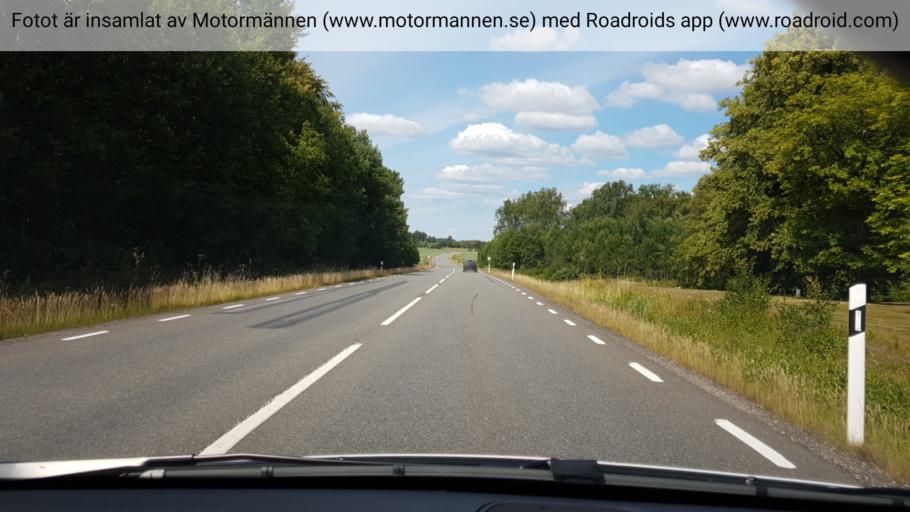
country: SE
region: Vaestra Goetaland
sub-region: Toreboda Kommun
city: Toereboda
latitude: 58.5670
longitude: 14.1094
